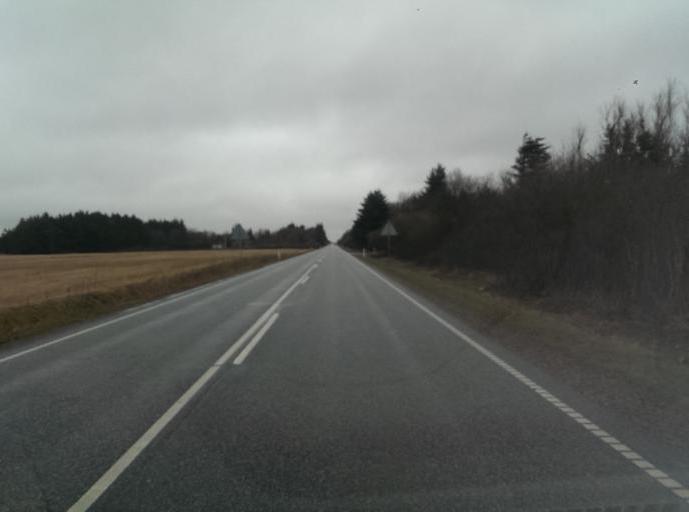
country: DK
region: Central Jutland
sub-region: Holstebro Kommune
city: Ulfborg
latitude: 56.2143
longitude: 8.3074
